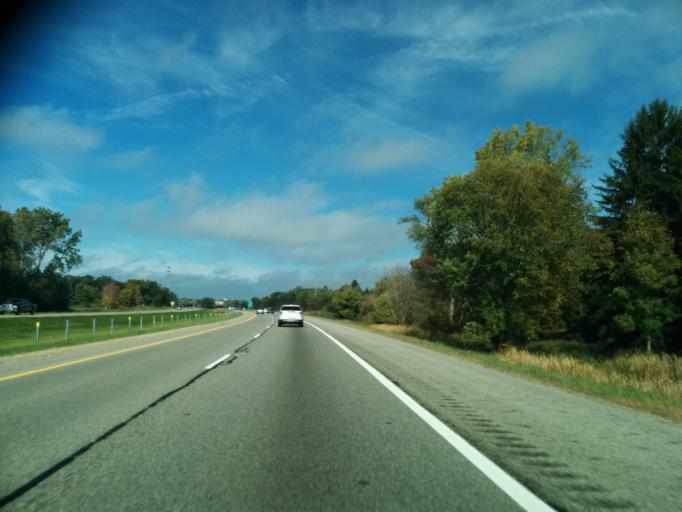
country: US
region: Michigan
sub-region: Livingston County
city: Brighton
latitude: 42.6105
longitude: -83.7421
